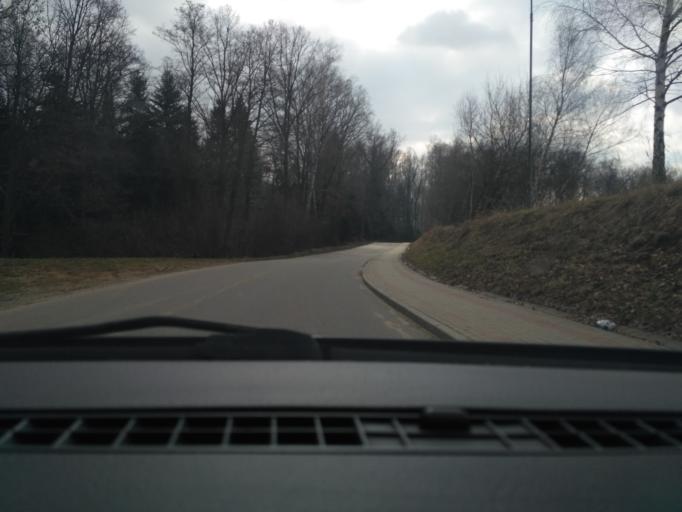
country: PL
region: Subcarpathian Voivodeship
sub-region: Powiat krosnienski
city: Kroscienko Wyzne
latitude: 49.6694
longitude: 21.8301
